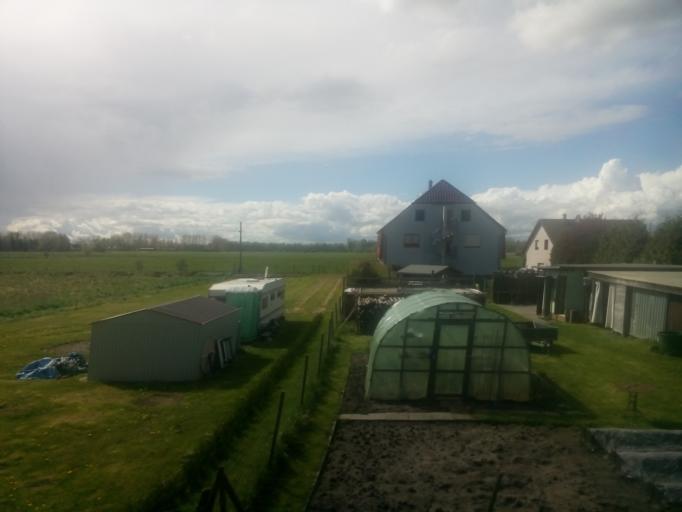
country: DE
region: Brandenburg
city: Kremmen
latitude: 52.7726
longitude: 13.0398
